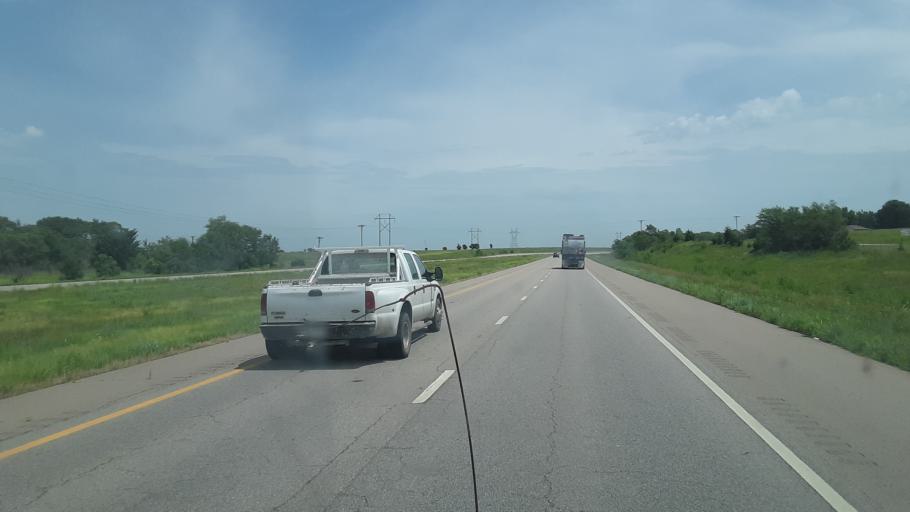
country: US
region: Kansas
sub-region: Butler County
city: Towanda
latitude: 37.8016
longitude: -97.0040
